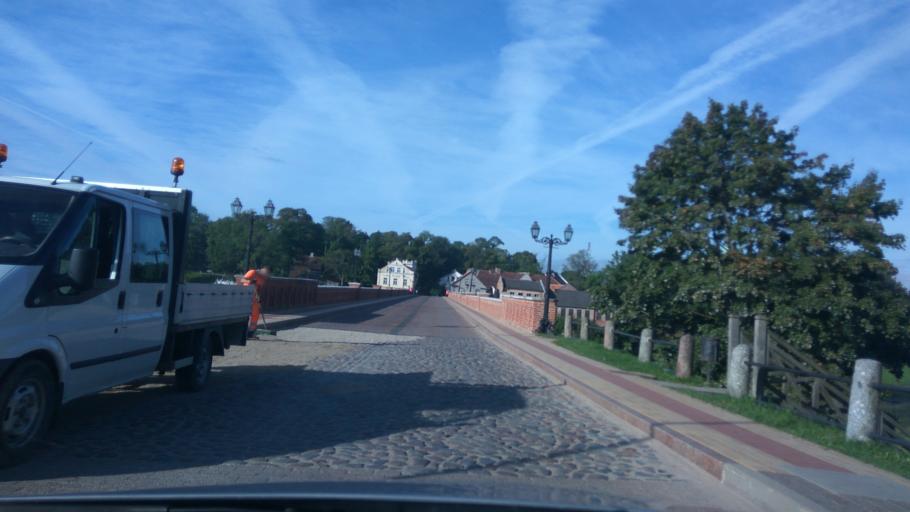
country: LV
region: Kuldigas Rajons
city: Kuldiga
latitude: 56.9706
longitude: 21.9792
